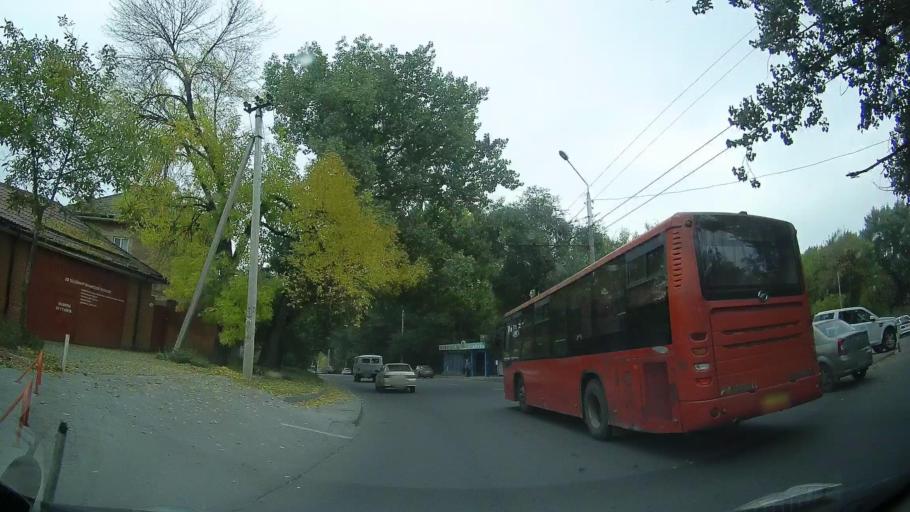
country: RU
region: Rostov
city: Severnyy
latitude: 47.2601
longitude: 39.6753
